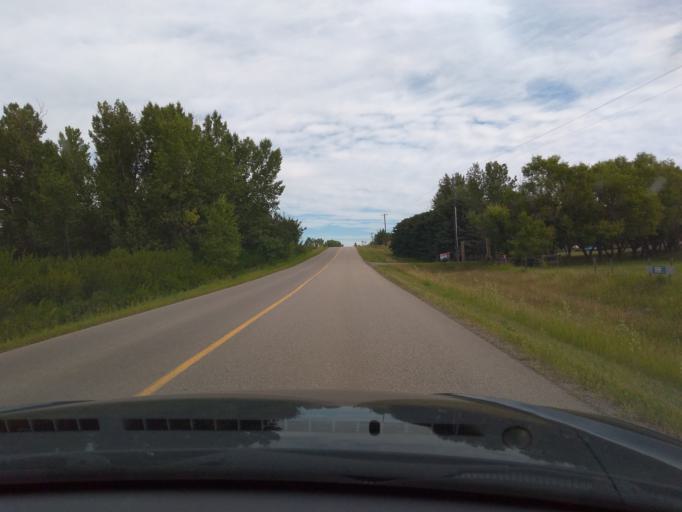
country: CA
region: Alberta
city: Didsbury
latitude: 51.6450
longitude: -114.1434
